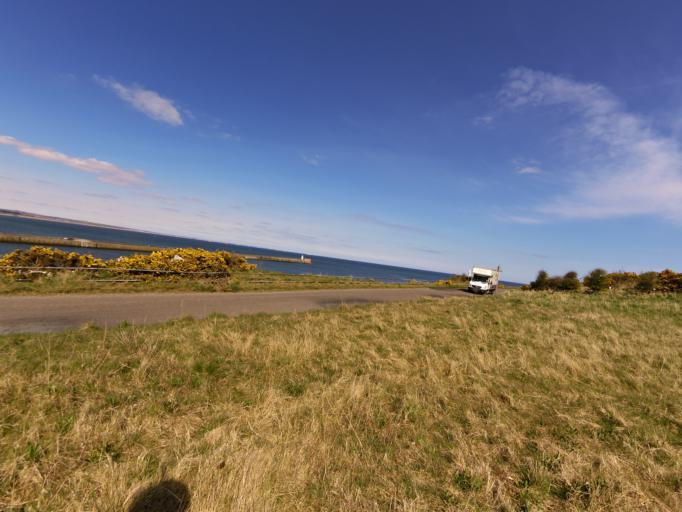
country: GB
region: Scotland
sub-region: Aberdeen City
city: Aberdeen
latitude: 57.1411
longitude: -2.0660
